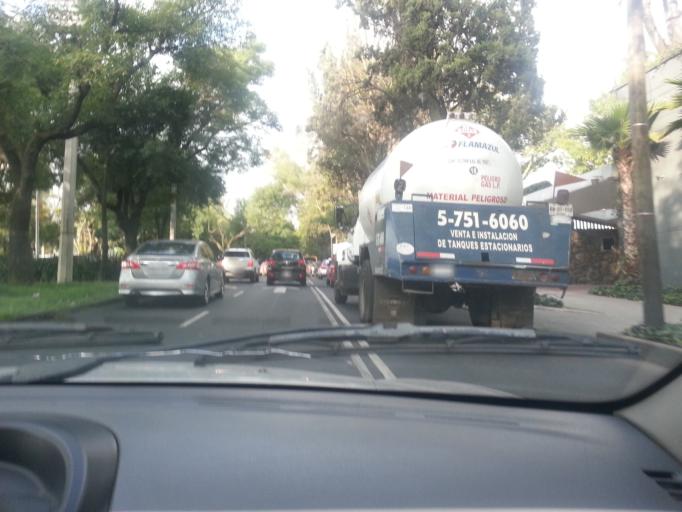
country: MX
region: Mexico City
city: Polanco
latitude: 19.4021
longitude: -99.2318
